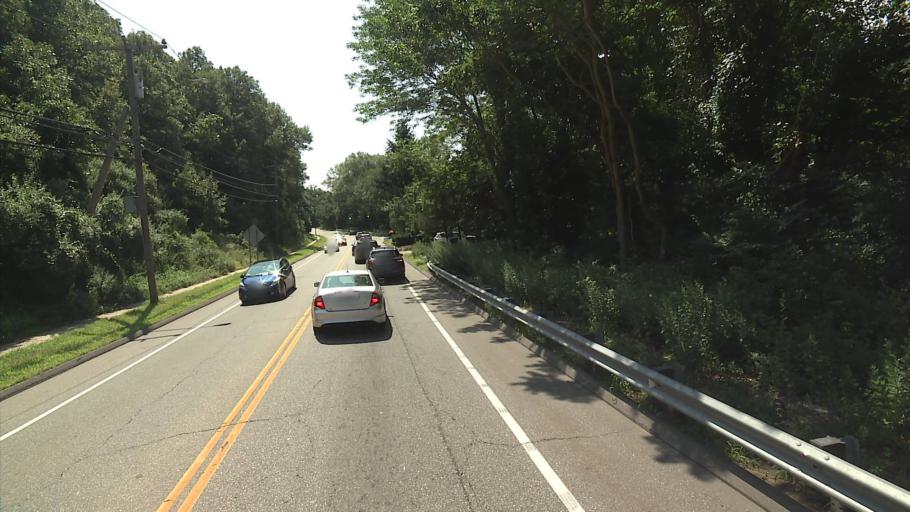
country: US
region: Connecticut
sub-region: New London County
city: Niantic
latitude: 41.3361
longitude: -72.2069
